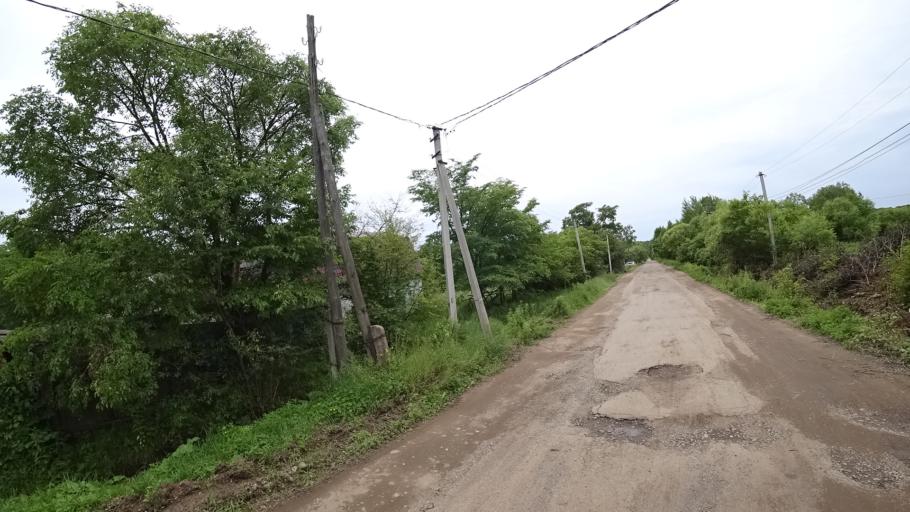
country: RU
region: Primorskiy
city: Novosysoyevka
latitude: 44.2071
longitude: 133.3306
